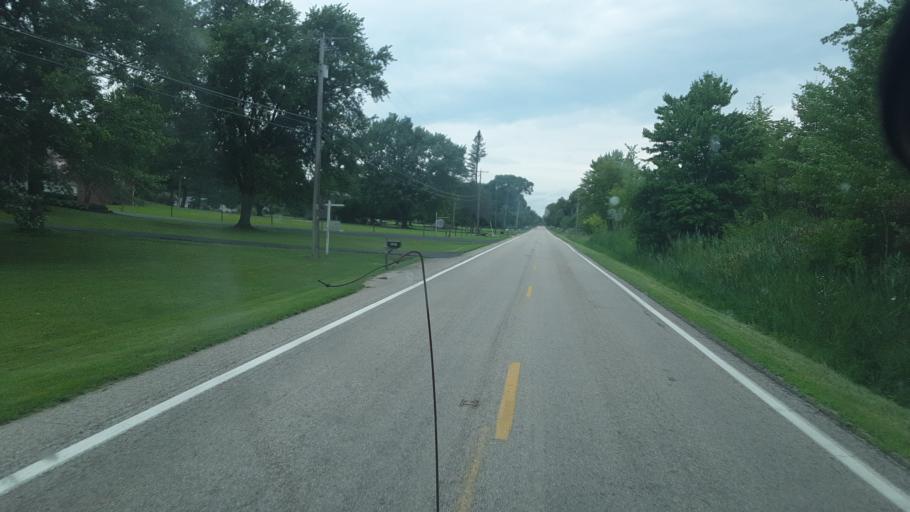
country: US
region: Ohio
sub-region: Trumbull County
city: Cortland
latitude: 41.3711
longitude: -80.6656
